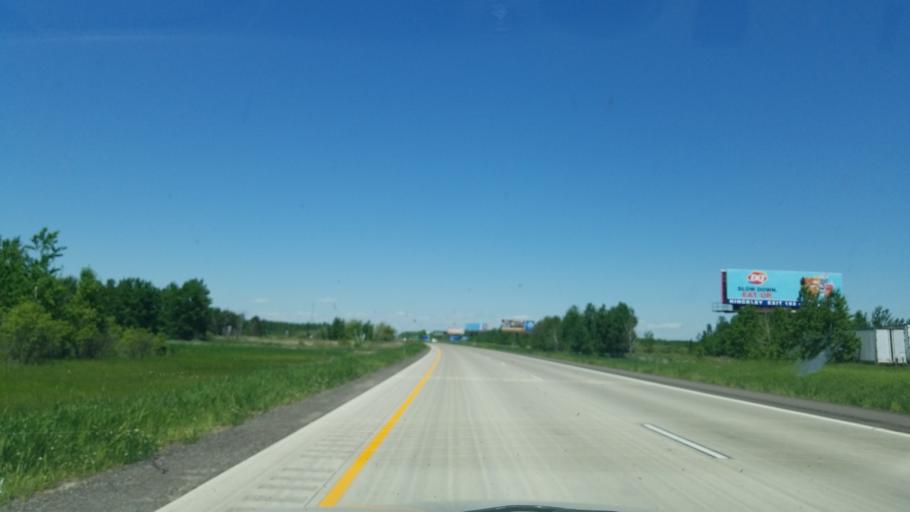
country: US
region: Minnesota
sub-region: Pine County
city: Pine City
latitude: 45.8913
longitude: -92.9669
